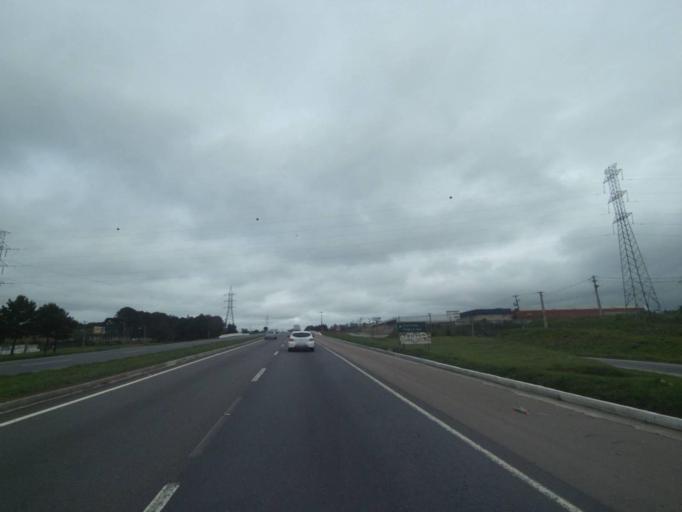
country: BR
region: Parana
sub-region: Araucaria
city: Araucaria
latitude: -25.5528
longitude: -49.3345
